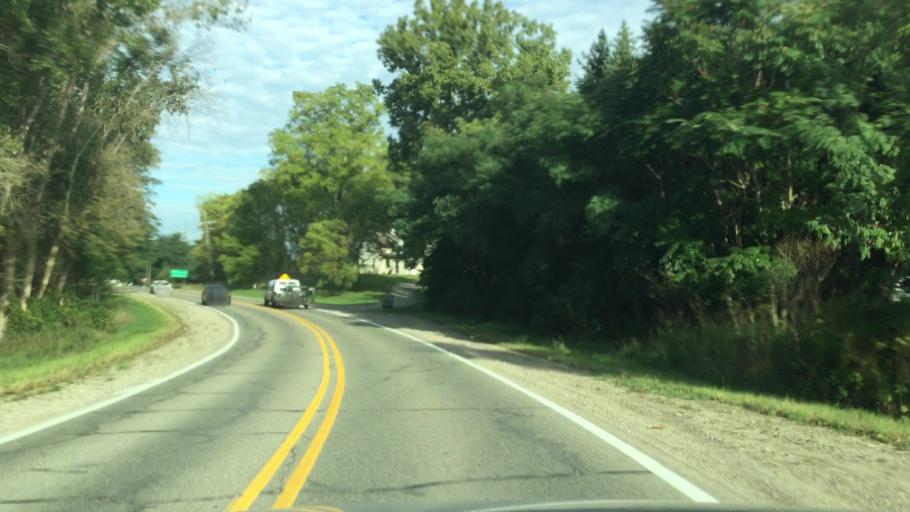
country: US
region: Michigan
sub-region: Livingston County
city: Brighton
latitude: 42.5355
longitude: -83.8684
